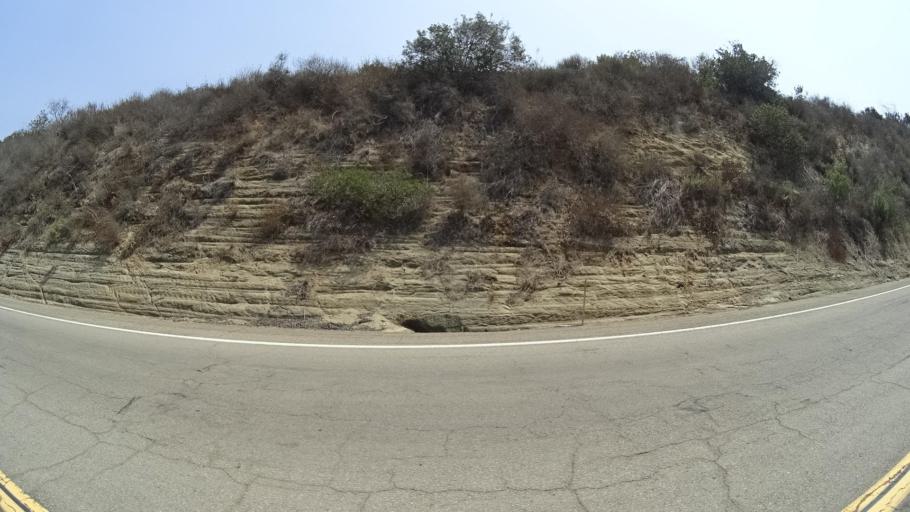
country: US
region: California
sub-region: San Diego County
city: Bonsall
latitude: 33.3025
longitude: -117.1528
